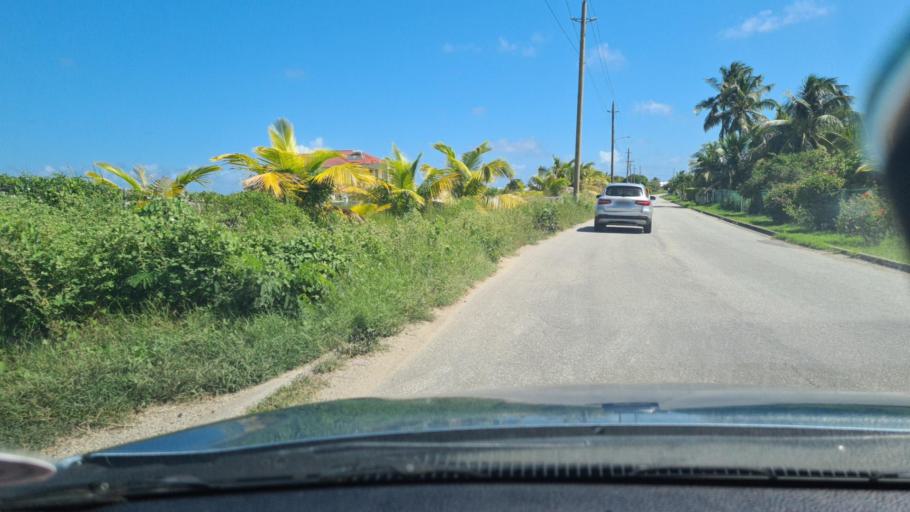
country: BB
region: Saint Philip
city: Crane
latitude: 13.1306
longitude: -59.4461
